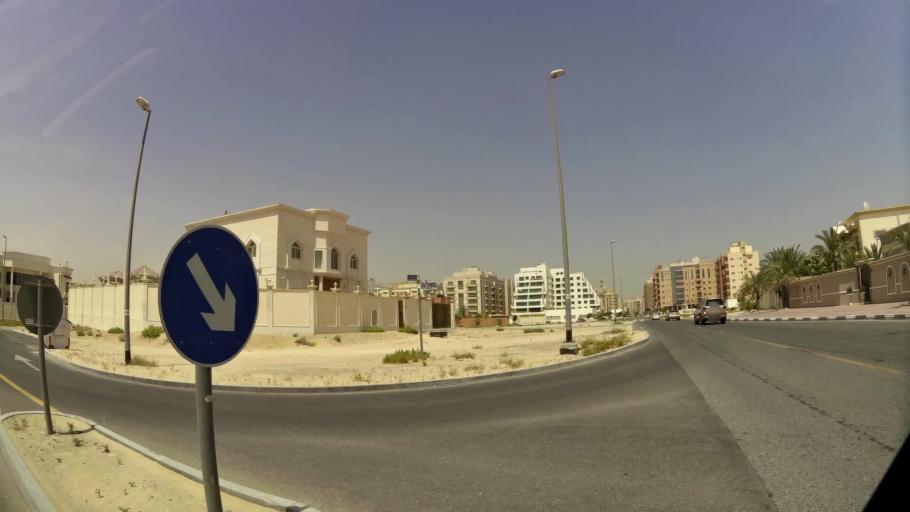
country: AE
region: Ash Shariqah
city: Sharjah
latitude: 25.1840
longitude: 55.4115
